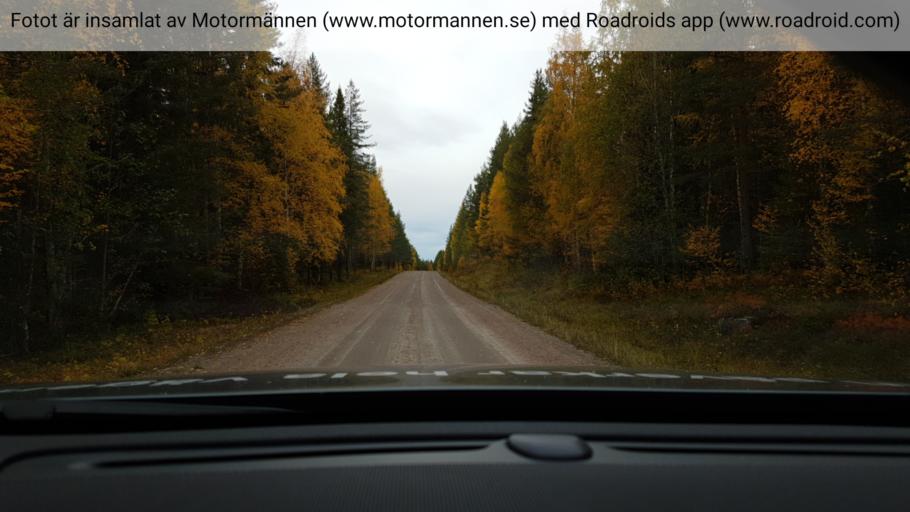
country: SE
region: Norrbotten
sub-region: Overkalix Kommun
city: OEverkalix
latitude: 66.2738
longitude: 22.9892
